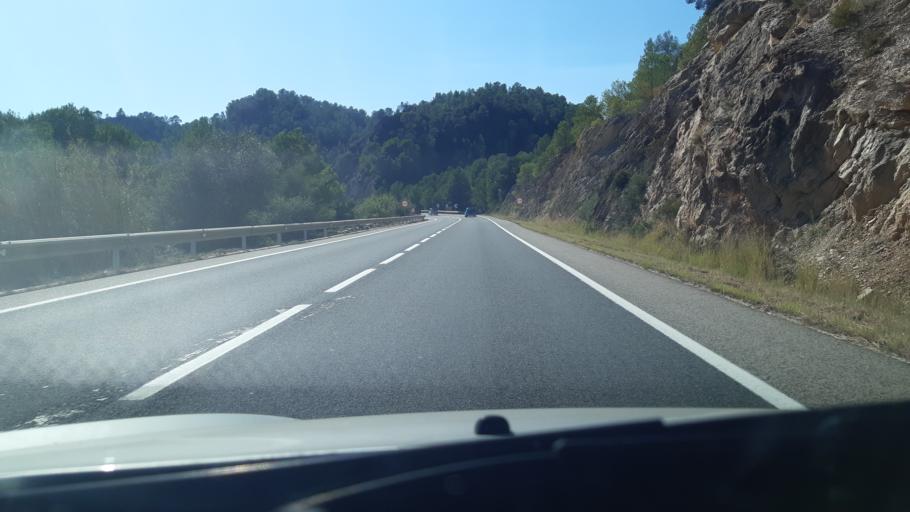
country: ES
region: Catalonia
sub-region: Provincia de Tarragona
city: Benifallet
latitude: 40.9550
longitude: 0.4849
